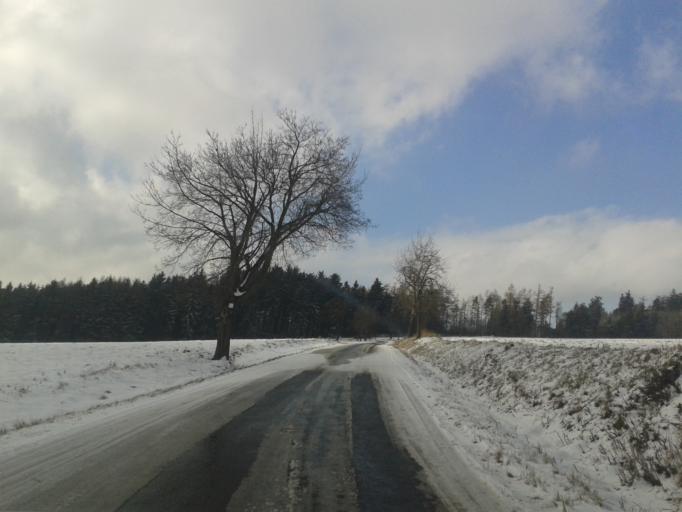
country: CZ
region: Olomoucky
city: Horni Stepanov
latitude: 49.5361
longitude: 16.8305
